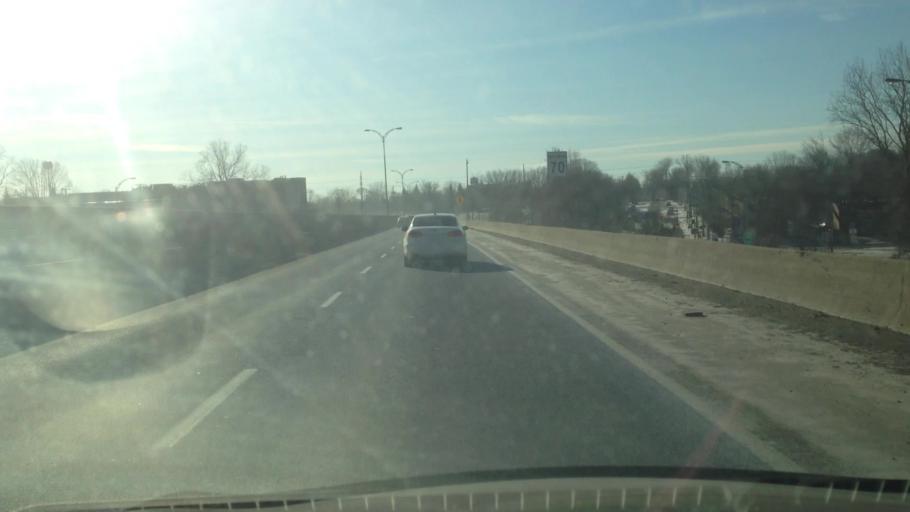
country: CA
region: Quebec
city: Montreal-Ouest
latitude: 45.4357
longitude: -73.6503
